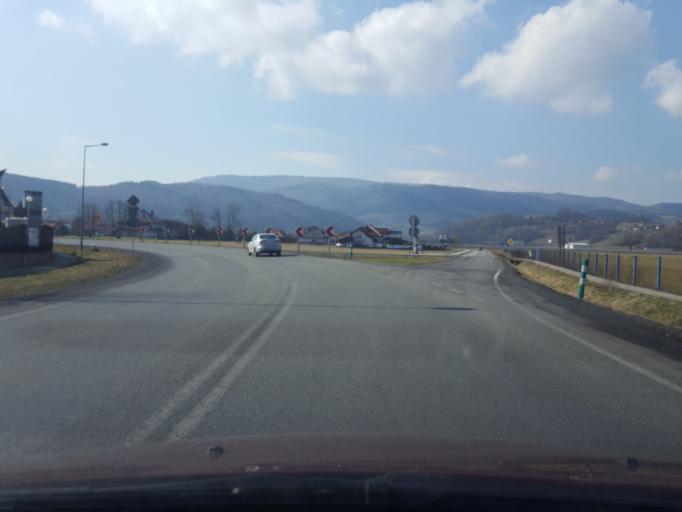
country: PL
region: Lesser Poland Voivodeship
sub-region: Powiat nowosadecki
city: Lososina Dolna
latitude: 49.7438
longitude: 20.6241
